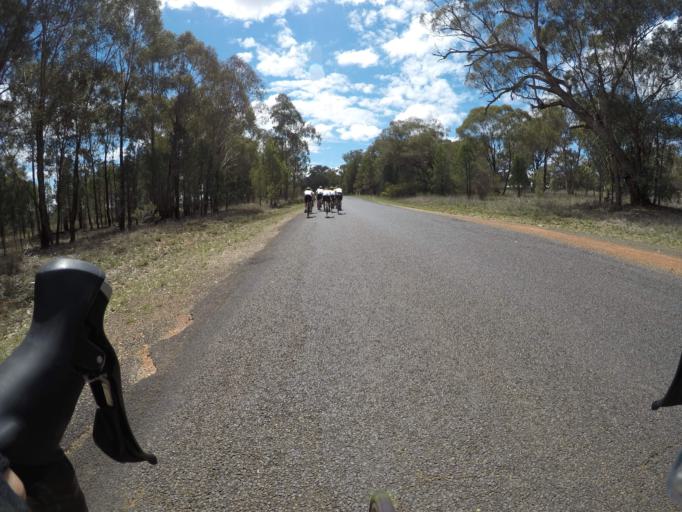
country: AU
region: New South Wales
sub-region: Dubbo Municipality
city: Dubbo
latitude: -32.3795
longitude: 148.5772
